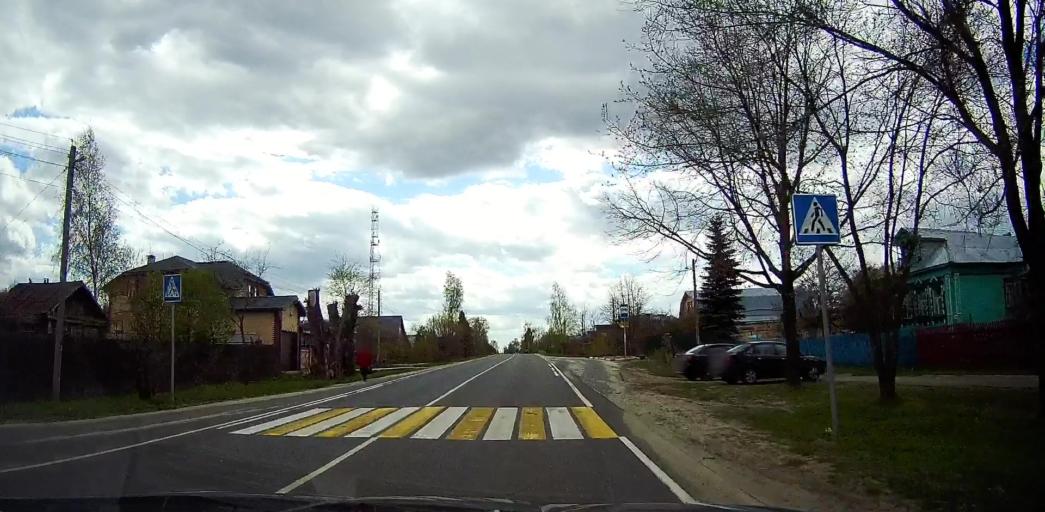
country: RU
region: Moskovskaya
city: Drezna
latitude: 55.6706
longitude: 38.7666
